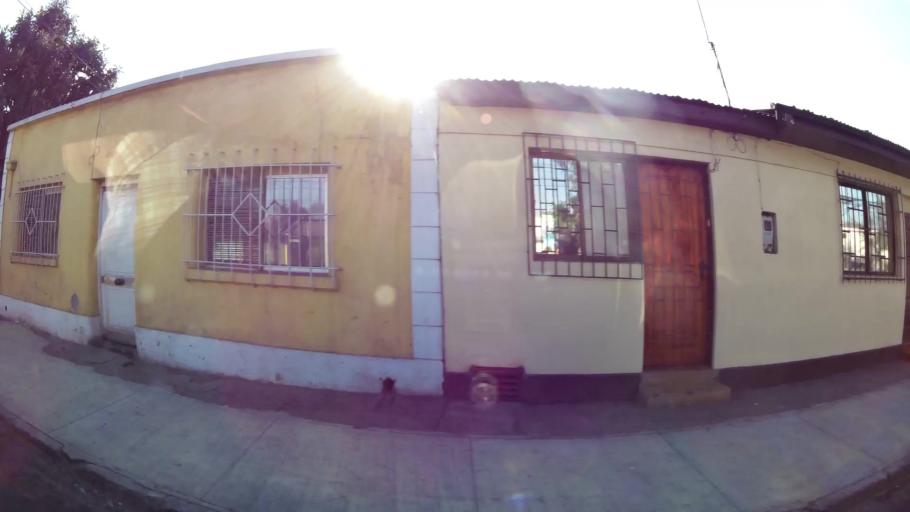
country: CL
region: Santiago Metropolitan
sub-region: Provincia de Santiago
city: Santiago
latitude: -33.3897
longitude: -70.6705
